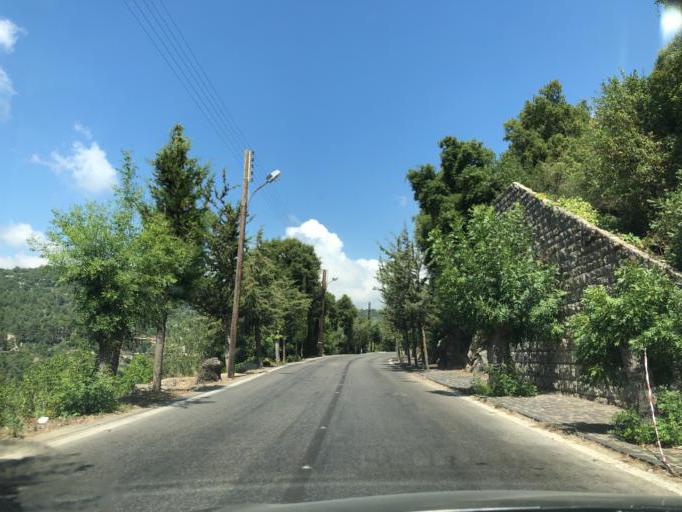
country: LB
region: Mont-Liban
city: Beit ed Dine
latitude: 33.6960
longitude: 35.5839
